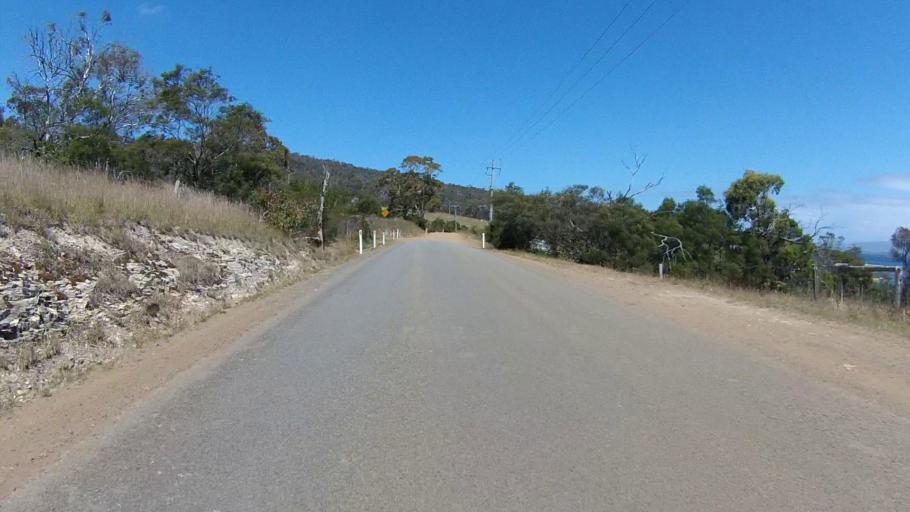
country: AU
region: Tasmania
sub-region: Clarence
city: Lauderdale
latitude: -42.9292
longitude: 147.4657
